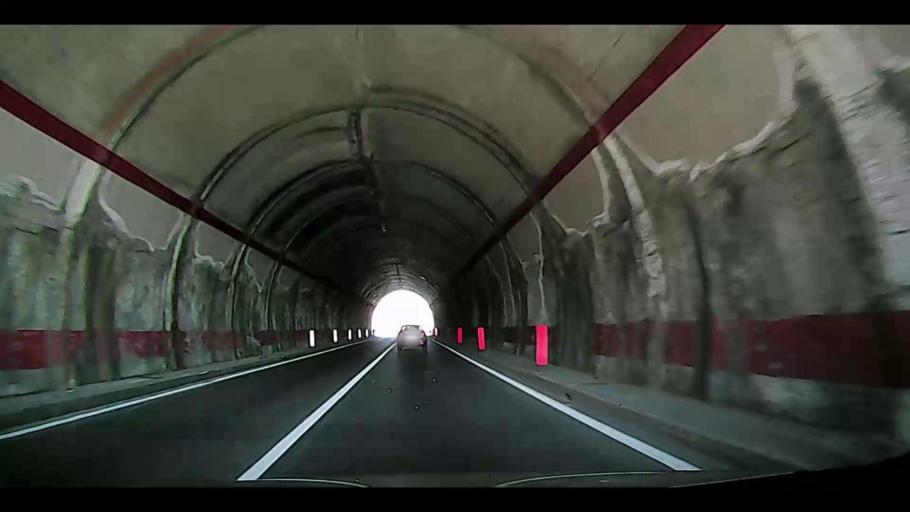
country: IT
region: Calabria
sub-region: Provincia di Crotone
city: Caccuri
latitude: 39.2193
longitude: 16.7950
